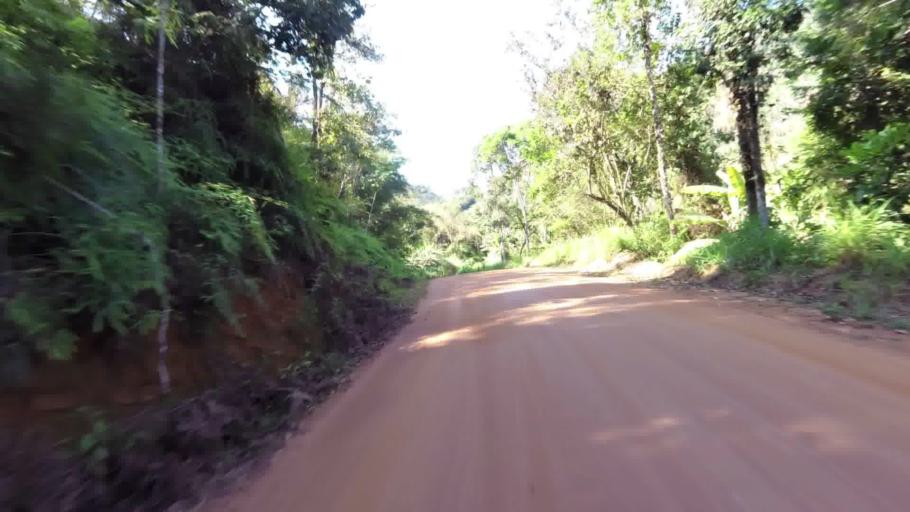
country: BR
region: Espirito Santo
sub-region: Alfredo Chaves
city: Alfredo Chaves
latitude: -20.5723
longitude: -40.7870
